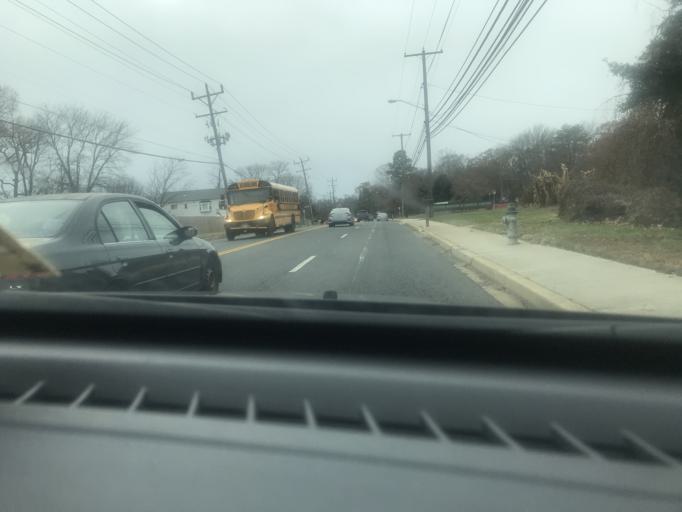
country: US
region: Maryland
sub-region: Prince George's County
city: Temple Hills
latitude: 38.7801
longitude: -76.9474
